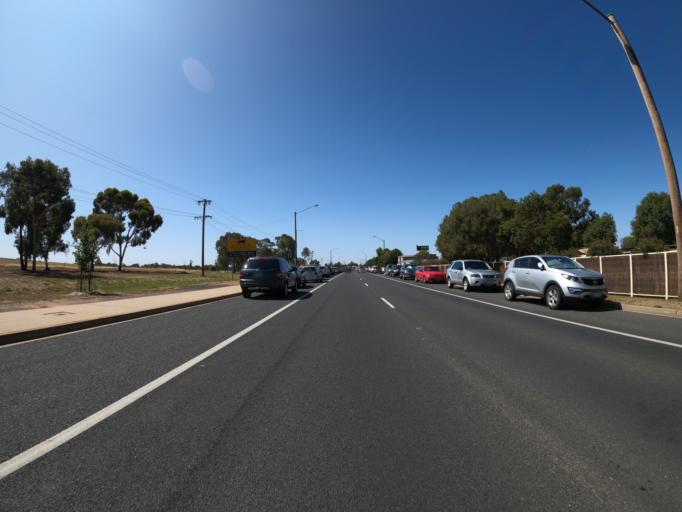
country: AU
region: New South Wales
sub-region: Corowa Shire
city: Mulwala
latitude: -35.9979
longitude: 146.0006
